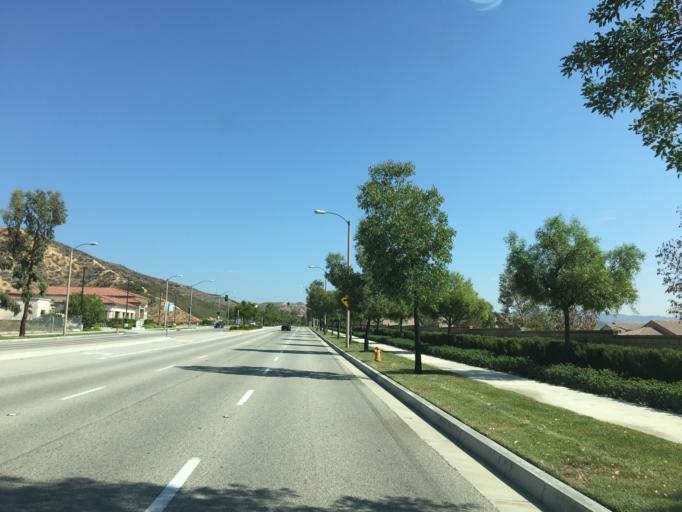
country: US
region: California
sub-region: Los Angeles County
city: Valencia
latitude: 34.4530
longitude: -118.5658
